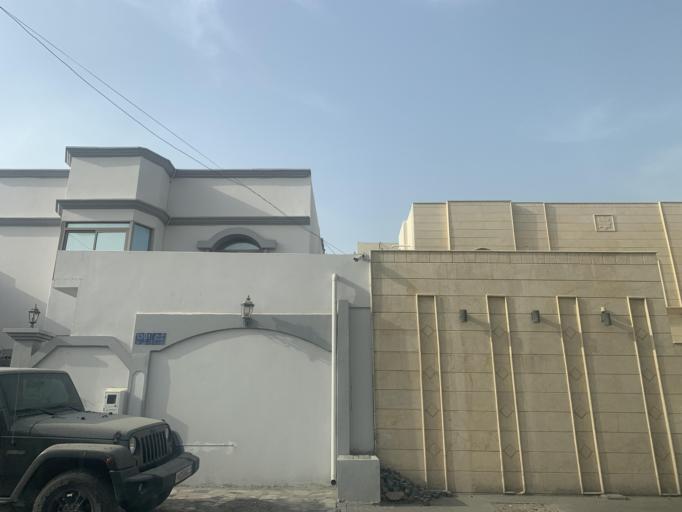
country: BH
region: Northern
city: Ar Rifa'
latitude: 26.1348
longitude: 50.5549
